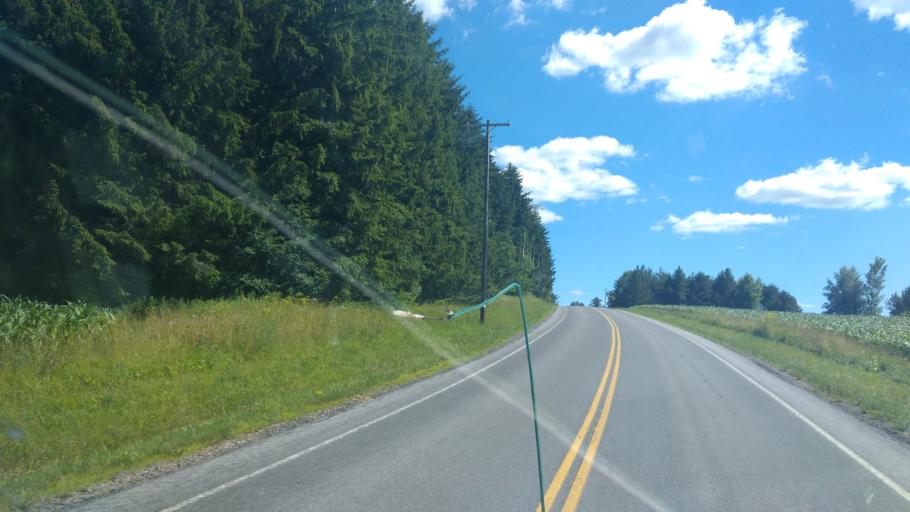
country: US
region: New York
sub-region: Wayne County
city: Lyons
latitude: 43.1298
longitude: -77.0148
